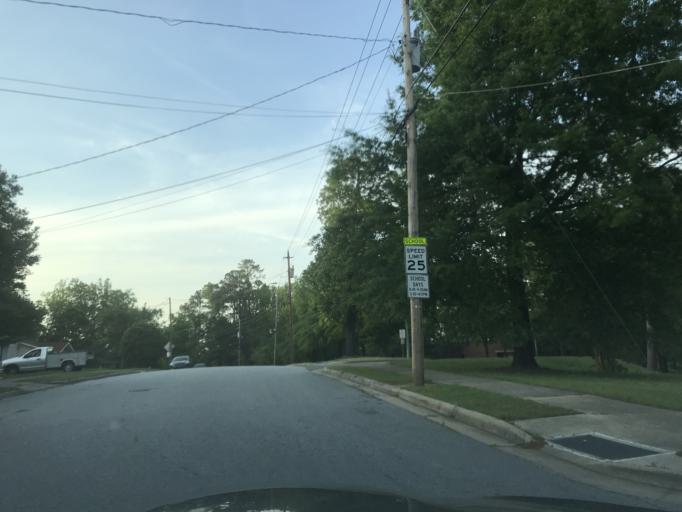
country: US
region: North Carolina
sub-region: Wake County
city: Raleigh
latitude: 35.7939
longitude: -78.6041
